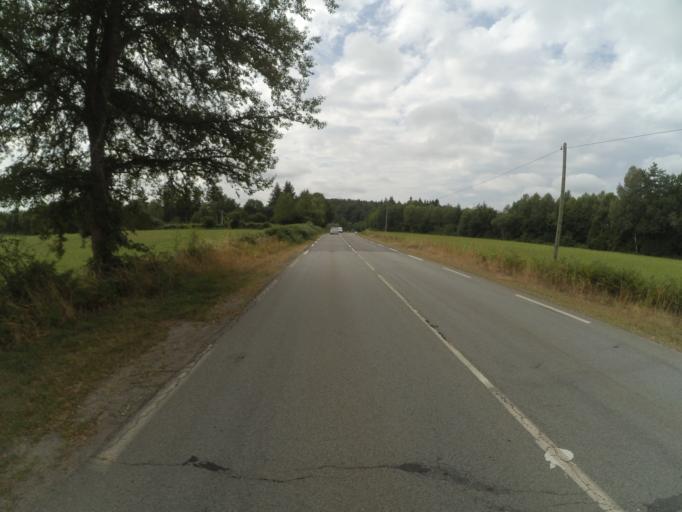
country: FR
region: Limousin
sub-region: Departement de la Correze
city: Ussel
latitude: 45.5871
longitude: 2.2916
